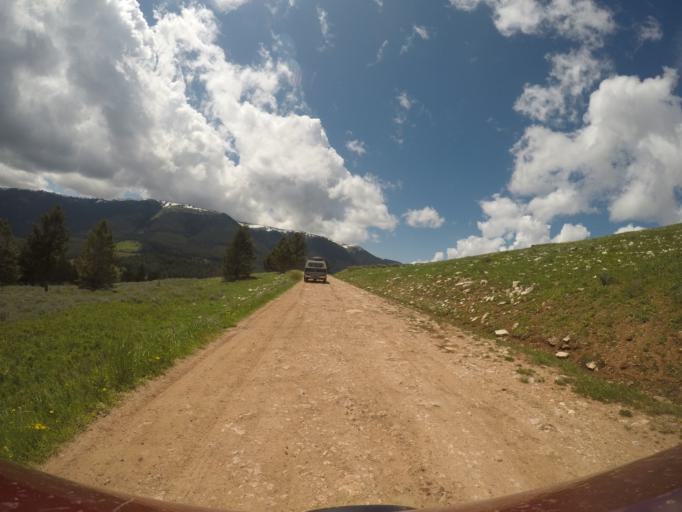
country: US
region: Wyoming
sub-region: Big Horn County
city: Lovell
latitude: 45.1759
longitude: -108.4357
